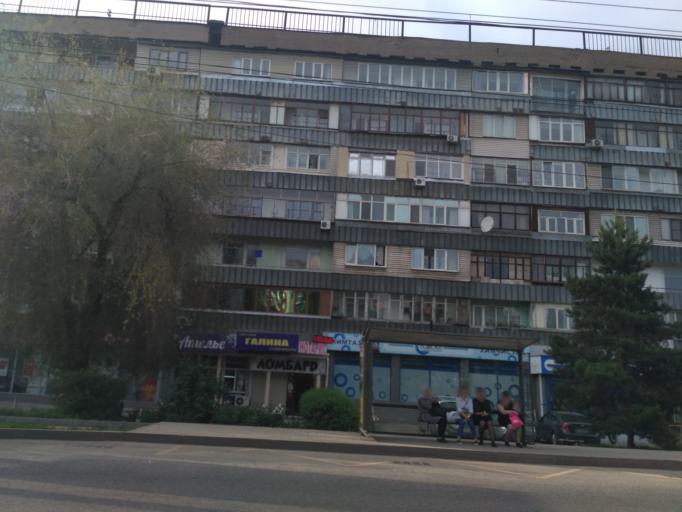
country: KZ
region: Almaty Qalasy
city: Almaty
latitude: 43.2393
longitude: 76.8976
